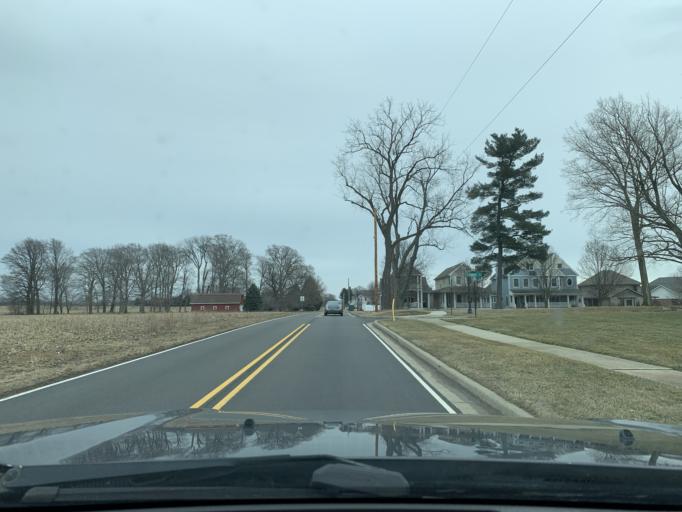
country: US
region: Indiana
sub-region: Porter County
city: Chesterton
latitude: 41.5863
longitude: -87.0345
